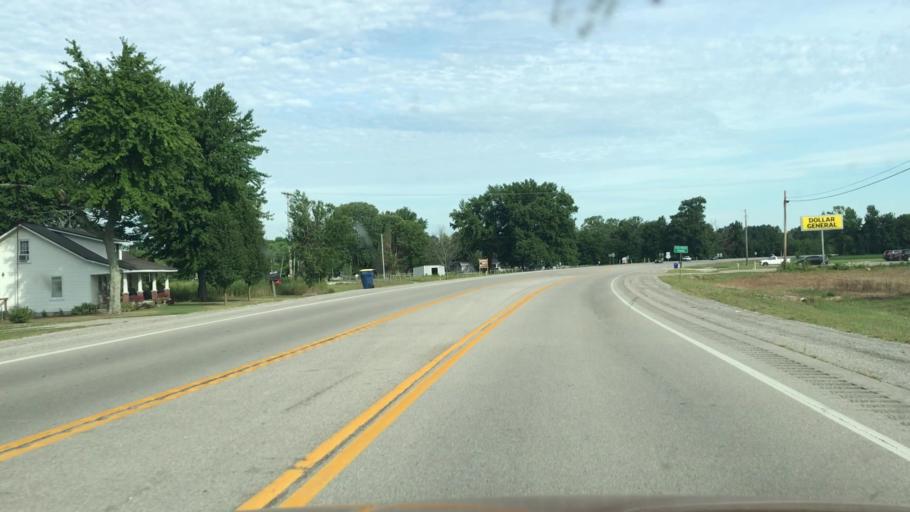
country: US
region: Kentucky
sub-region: Edmonson County
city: Brownsville
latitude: 37.1187
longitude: -86.2318
